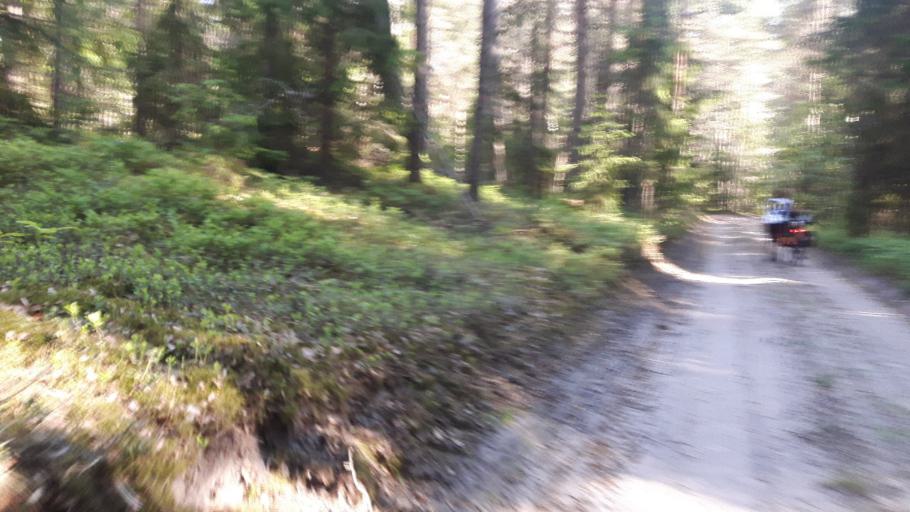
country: LV
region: Salacgrivas
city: Salacgriva
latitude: 57.7235
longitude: 24.3485
